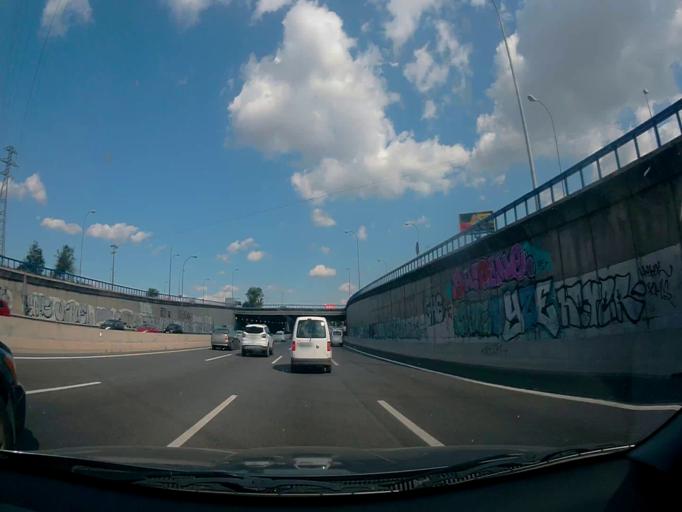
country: ES
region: Madrid
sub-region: Provincia de Madrid
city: Leganes
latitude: 40.3623
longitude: -3.7803
